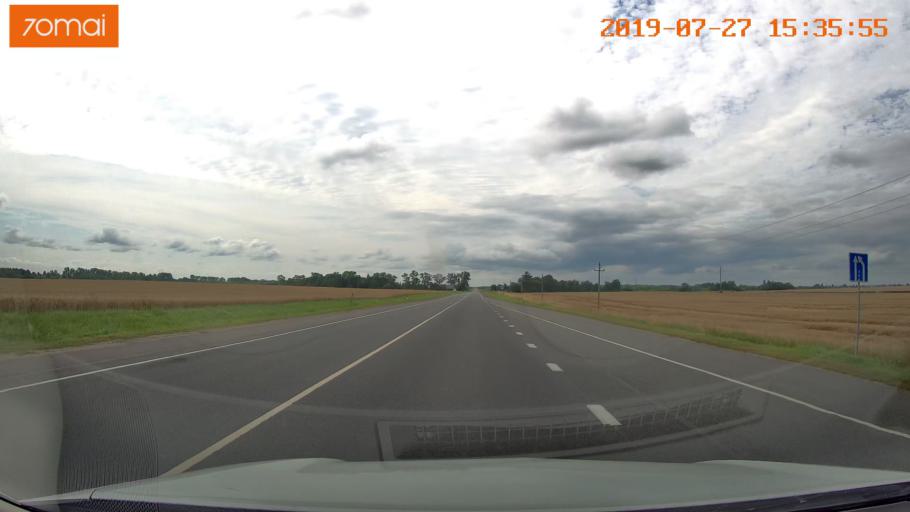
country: RU
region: Kaliningrad
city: Gusev
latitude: 54.6128
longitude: 22.3839
